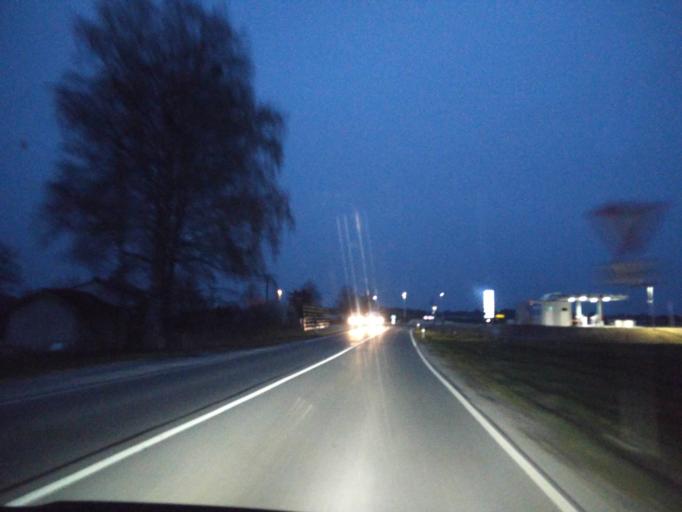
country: DE
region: Bavaria
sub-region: Upper Bavaria
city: Griesstatt
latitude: 47.9878
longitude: 12.1771
